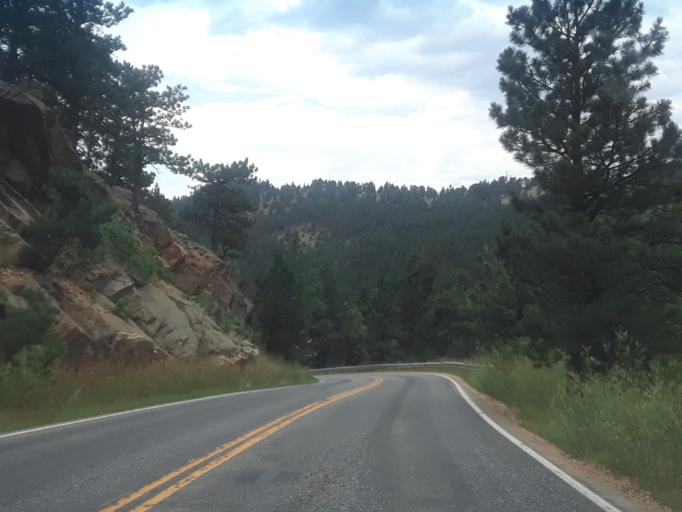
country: US
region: Colorado
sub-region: Boulder County
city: Boulder
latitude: 40.0307
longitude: -105.3155
